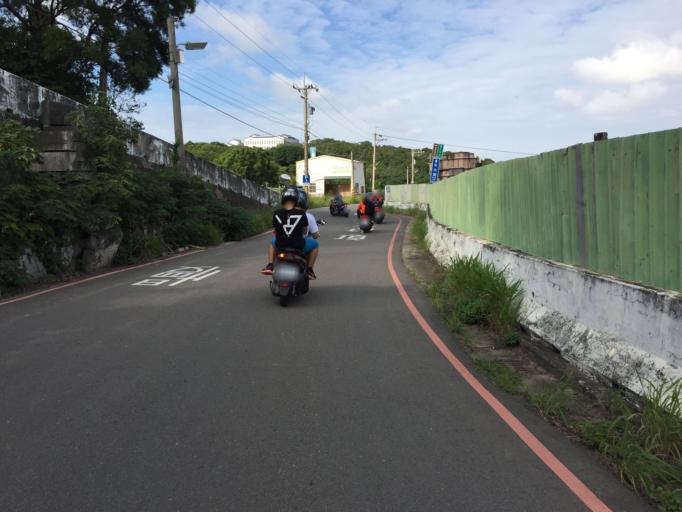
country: TW
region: Taiwan
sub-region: Hsinchu
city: Hsinchu
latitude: 24.7768
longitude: 120.9277
